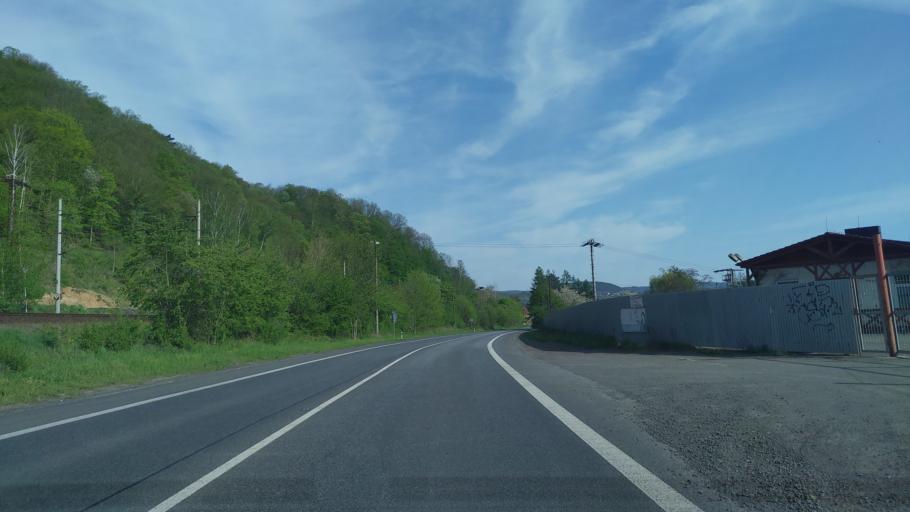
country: CZ
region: Ustecky
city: Povrly
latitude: 50.7223
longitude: 14.1874
